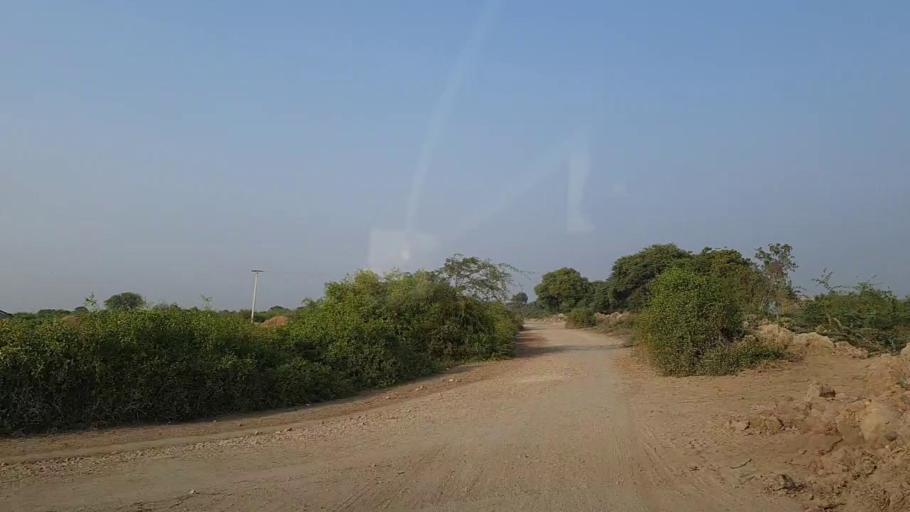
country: PK
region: Sindh
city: Thatta
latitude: 24.6916
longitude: 67.7923
